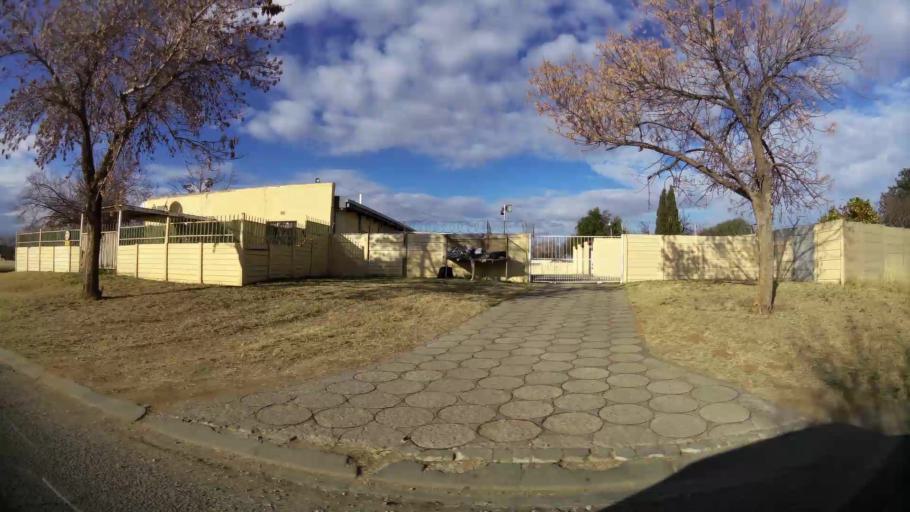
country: ZA
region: Orange Free State
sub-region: Lejweleputswa District Municipality
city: Welkom
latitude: -27.9784
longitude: 26.6960
